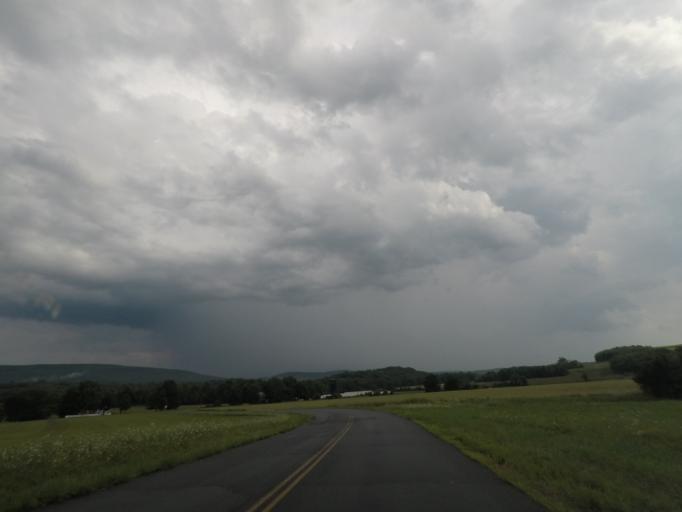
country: US
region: New York
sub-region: Rensselaer County
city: Poestenkill
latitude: 42.7179
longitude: -73.5801
